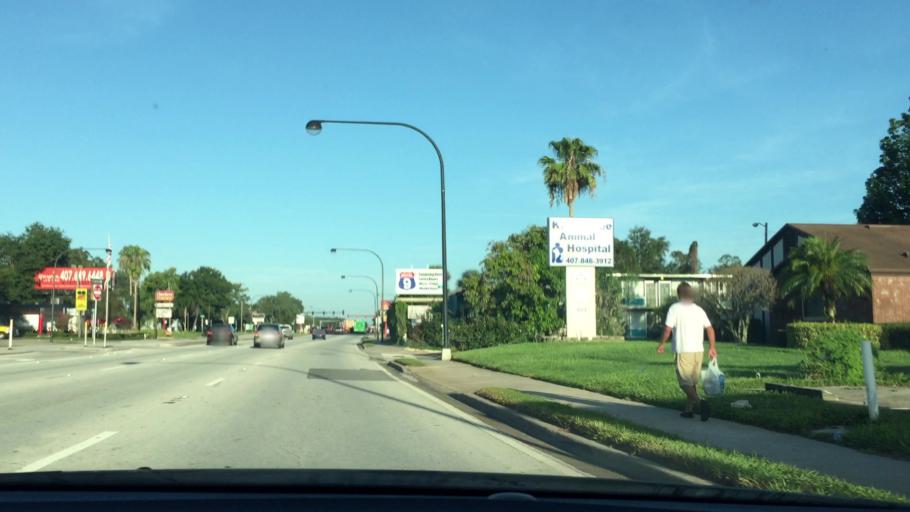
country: US
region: Florida
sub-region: Osceola County
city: Kissimmee
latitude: 28.3045
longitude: -81.4003
